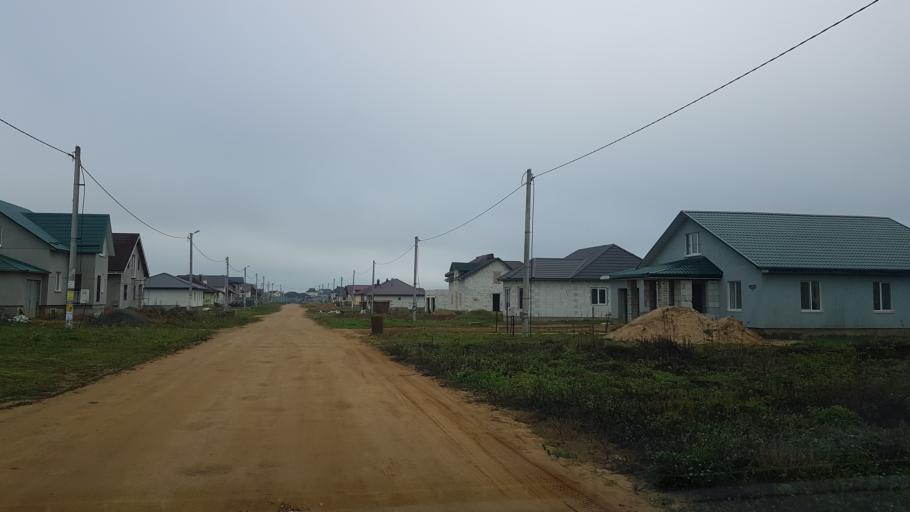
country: BY
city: Fanipol
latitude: 53.7299
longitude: 27.3274
